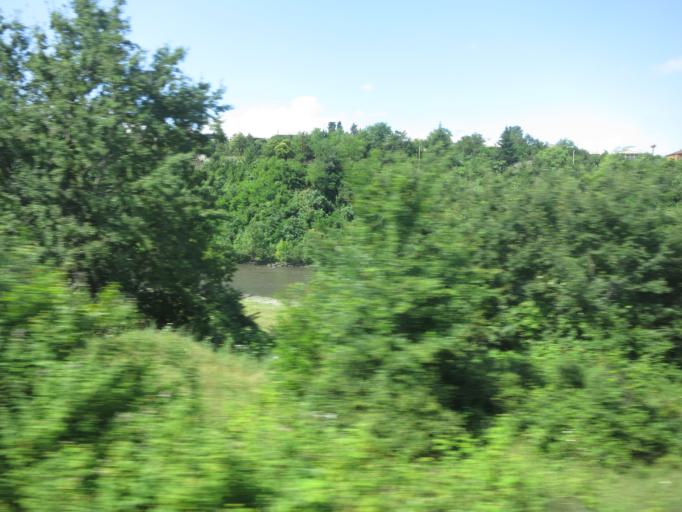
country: GE
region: Imereti
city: Zestap'oni
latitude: 42.1044
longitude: 43.0571
